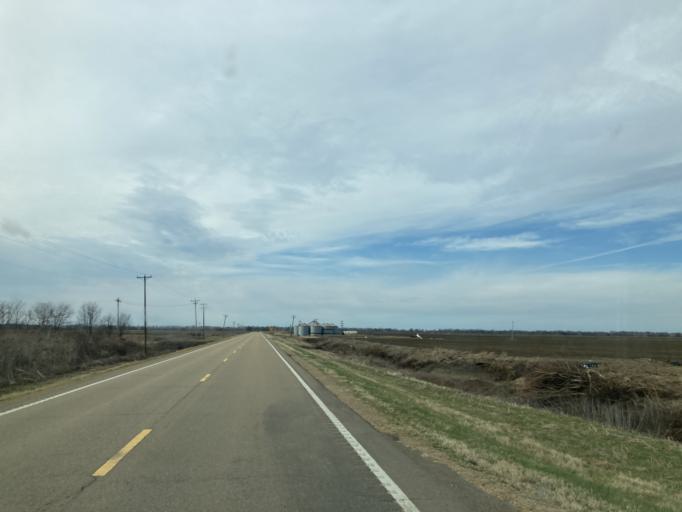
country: US
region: Mississippi
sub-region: Humphreys County
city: Belzoni
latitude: 33.1828
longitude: -90.6457
